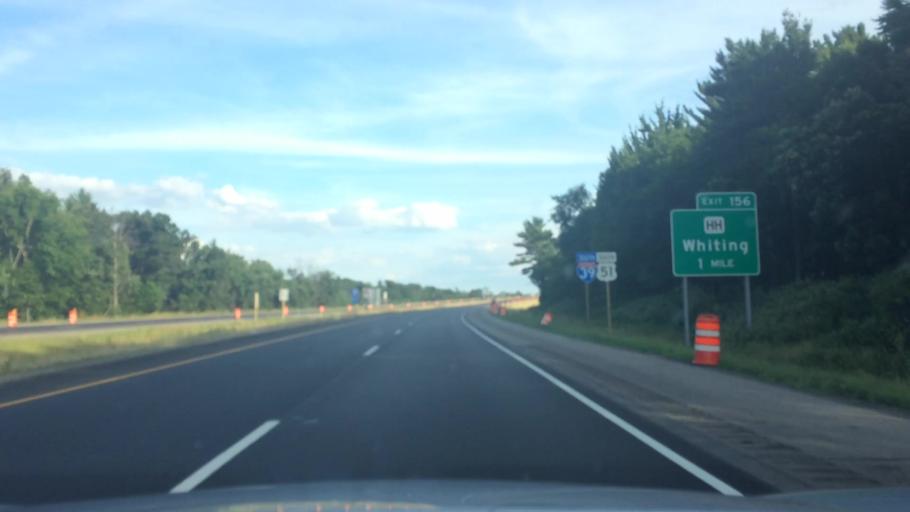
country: US
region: Wisconsin
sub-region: Portage County
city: Whiting
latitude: 44.5183
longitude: -89.5228
